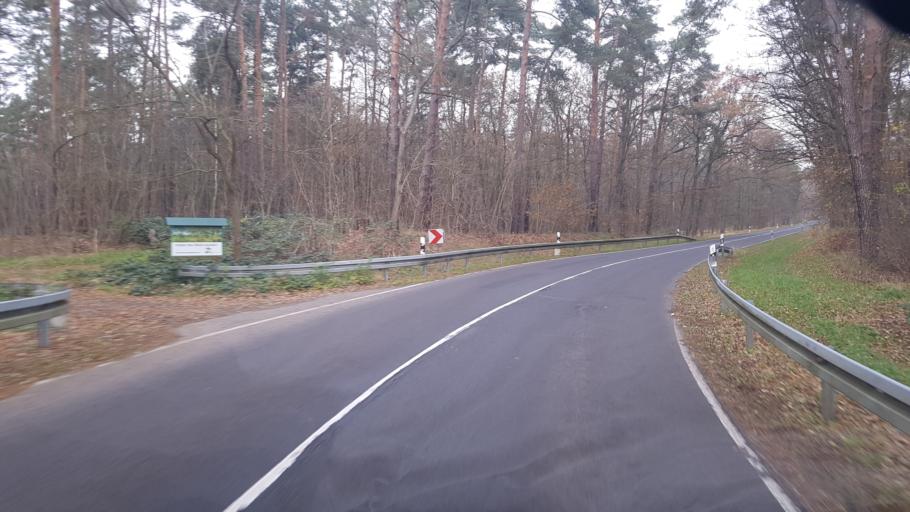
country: DE
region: Brandenburg
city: Schenkendobern
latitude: 51.9425
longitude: 14.6323
